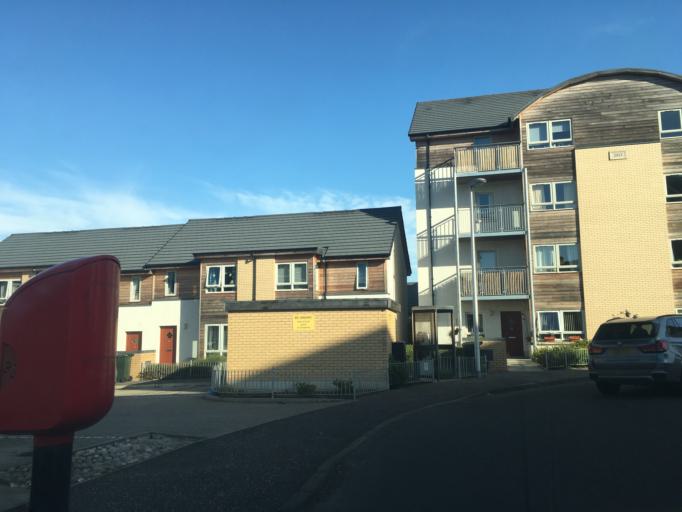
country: GB
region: Scotland
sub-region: Edinburgh
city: Colinton
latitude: 55.9106
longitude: -3.2236
